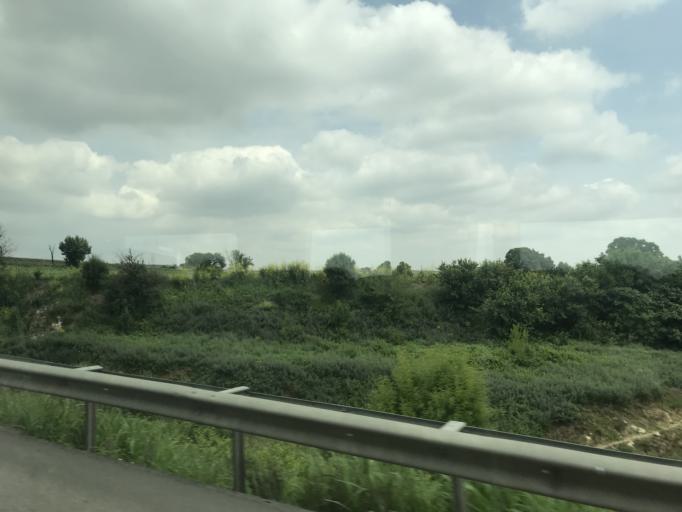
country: TR
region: Tekirdag
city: Tekirdag
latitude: 41.0034
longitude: 27.5429
